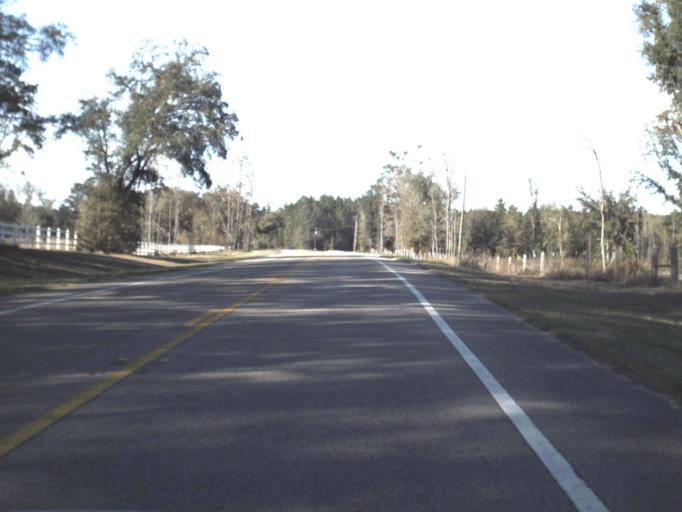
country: US
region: Florida
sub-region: Jackson County
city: Marianna
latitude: 30.6196
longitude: -85.1806
